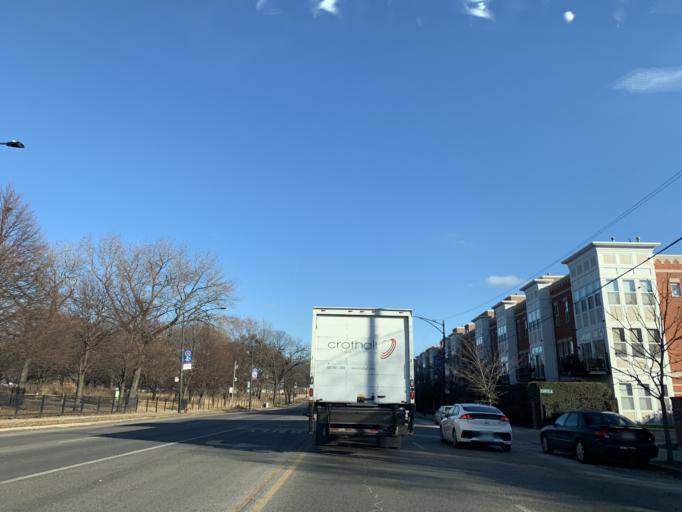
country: US
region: Illinois
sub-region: Cook County
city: Lincolnwood
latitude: 41.9539
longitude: -87.6973
